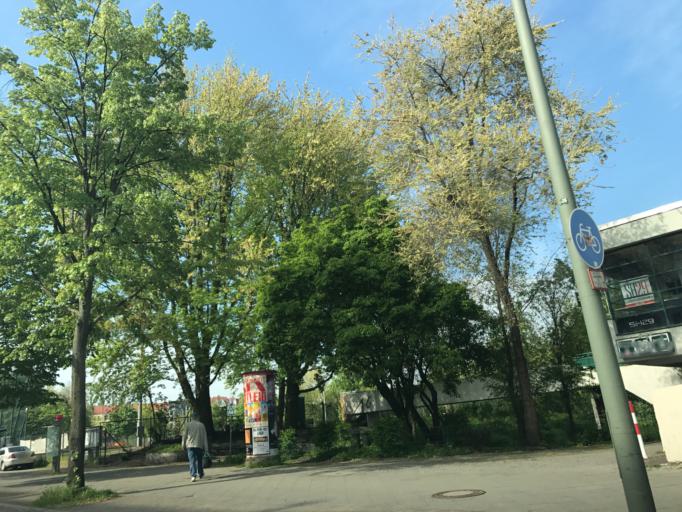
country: DE
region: Berlin
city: Charlottenburg-Nord
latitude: 52.5233
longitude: 13.3059
